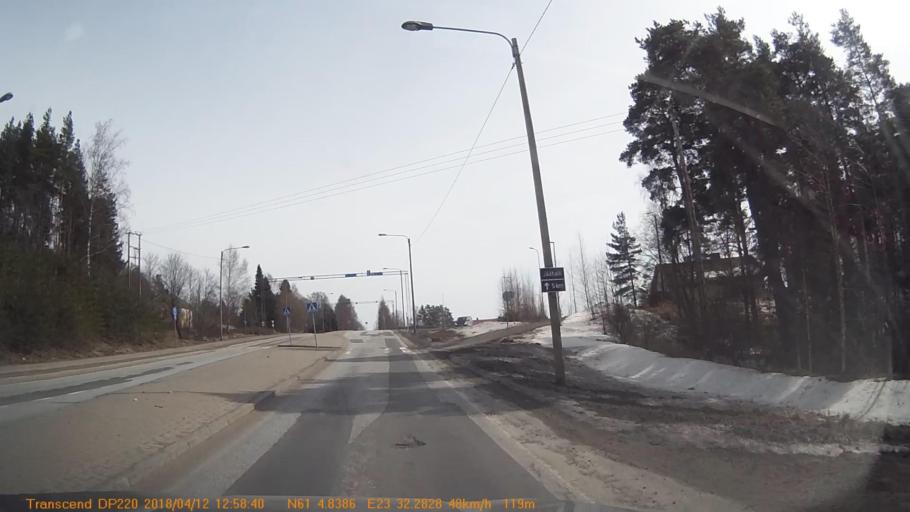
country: FI
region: Pirkanmaa
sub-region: Etelae-Pirkanmaa
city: Urjala
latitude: 61.0805
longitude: 23.5385
